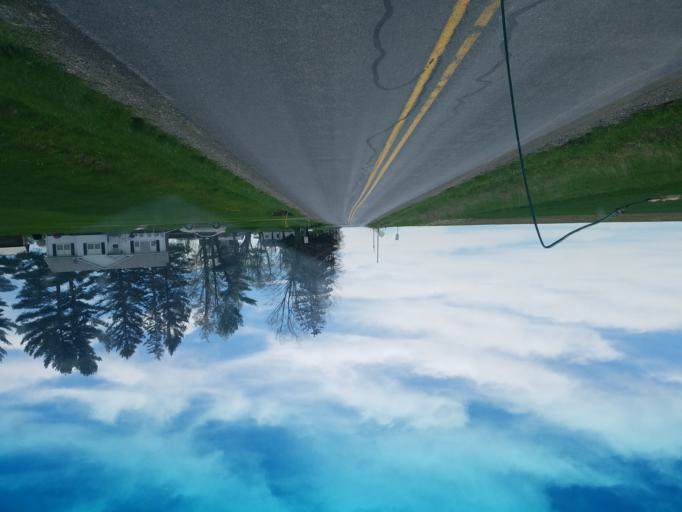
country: US
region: Pennsylvania
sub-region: Tioga County
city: Wellsboro
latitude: 41.7277
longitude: -77.3882
